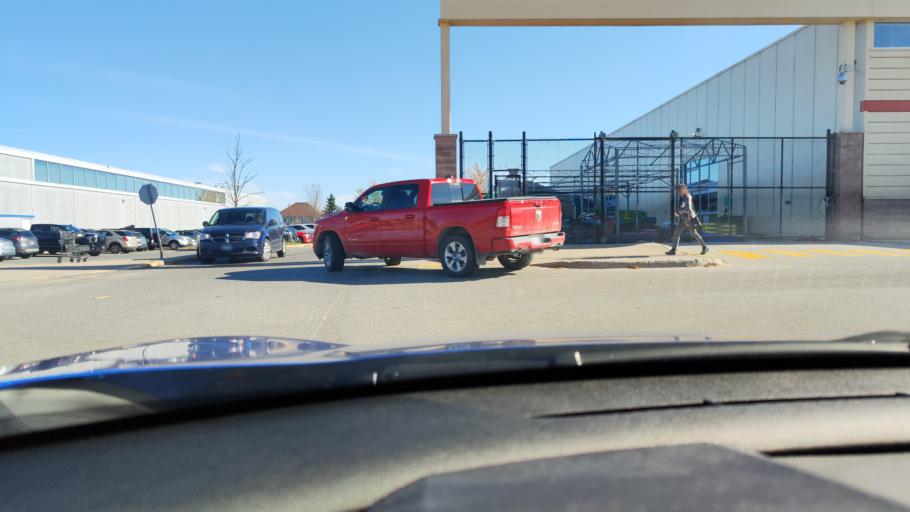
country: CA
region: Ontario
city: Wasaga Beach
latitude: 44.4723
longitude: -80.0745
